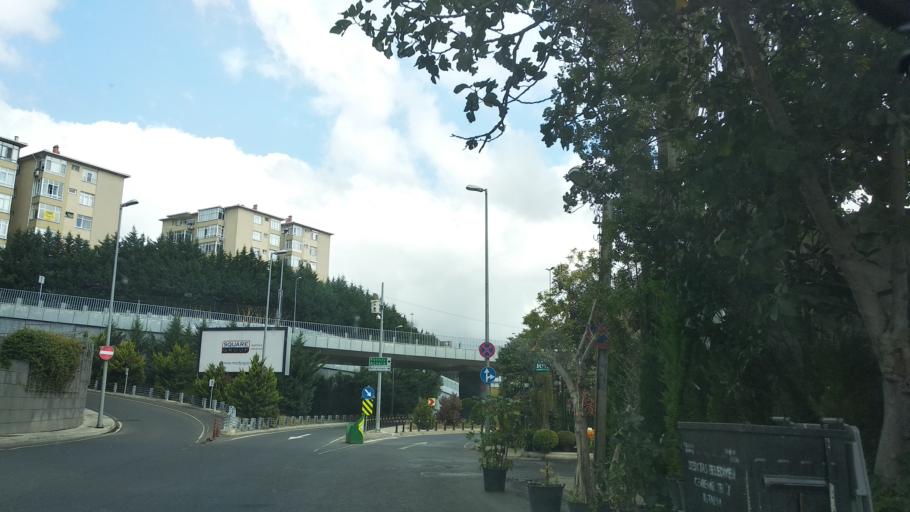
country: TR
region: Istanbul
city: Sisli
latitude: 41.0889
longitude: 29.0355
